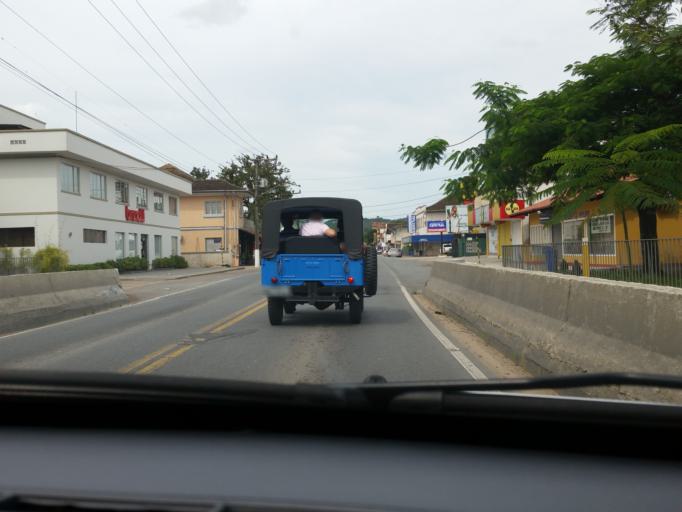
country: BR
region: Santa Catarina
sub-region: Rodeio
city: Gavea
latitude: -27.0348
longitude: -49.3887
